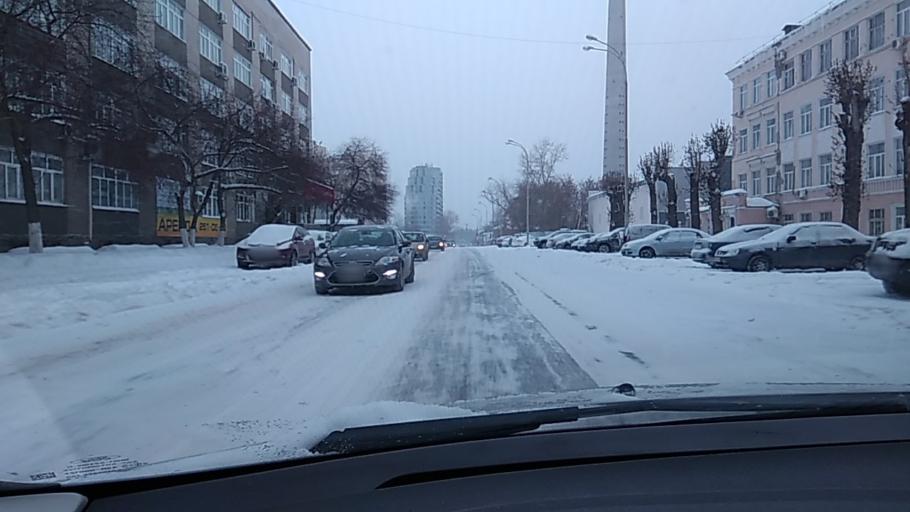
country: RU
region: Sverdlovsk
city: Yekaterinburg
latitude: 56.8206
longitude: 60.6087
